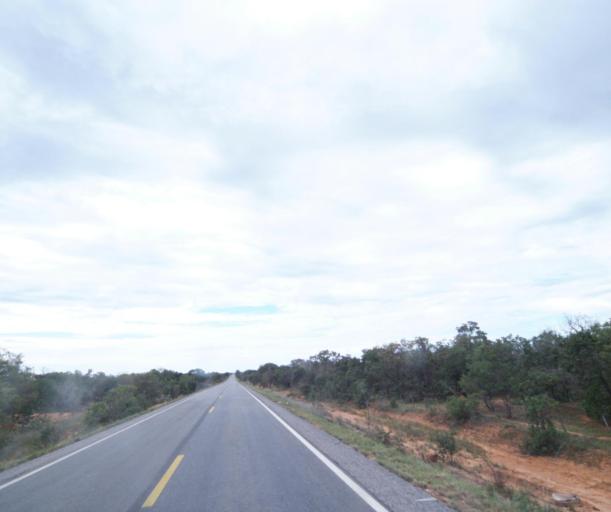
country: BR
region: Bahia
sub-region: Sao Felix Do Coribe
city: Santa Maria da Vitoria
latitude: -13.9728
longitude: -44.4463
